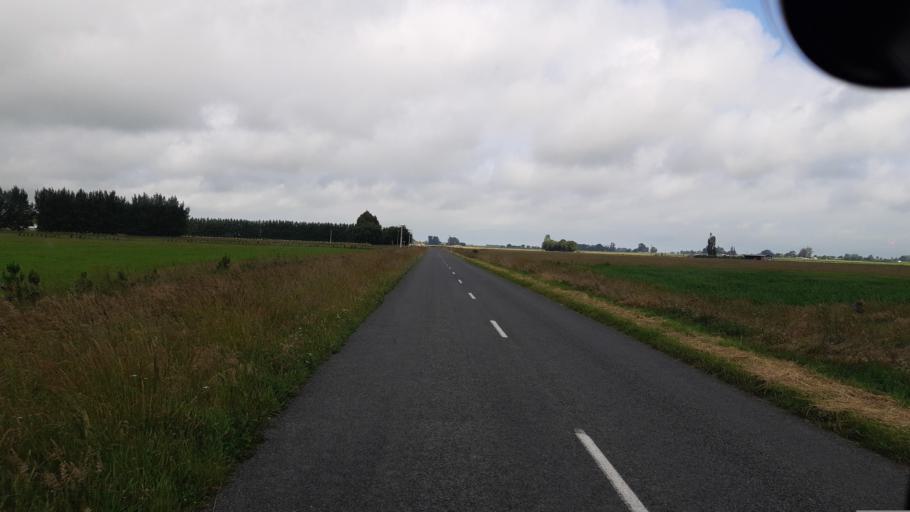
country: NZ
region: Canterbury
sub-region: Timaru District
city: Timaru
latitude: -44.2438
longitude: 171.3111
